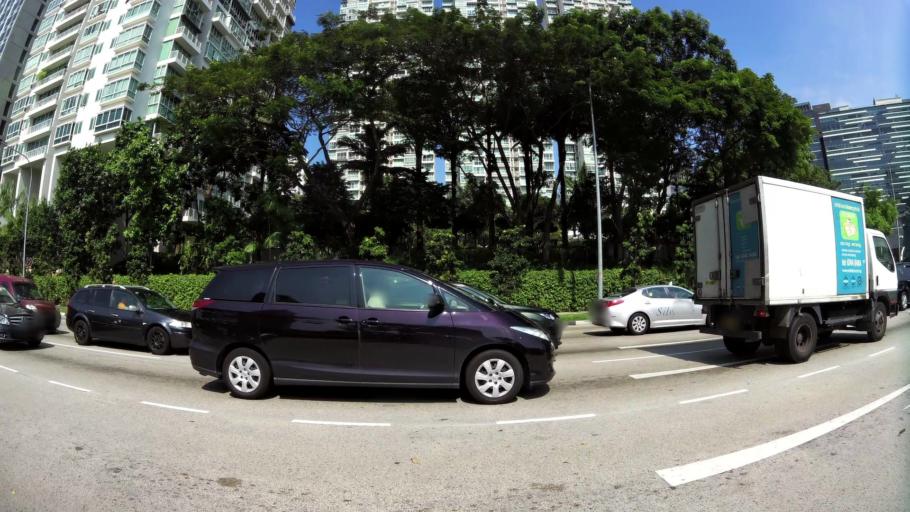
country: SG
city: Singapore
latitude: 1.3082
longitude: 103.8637
